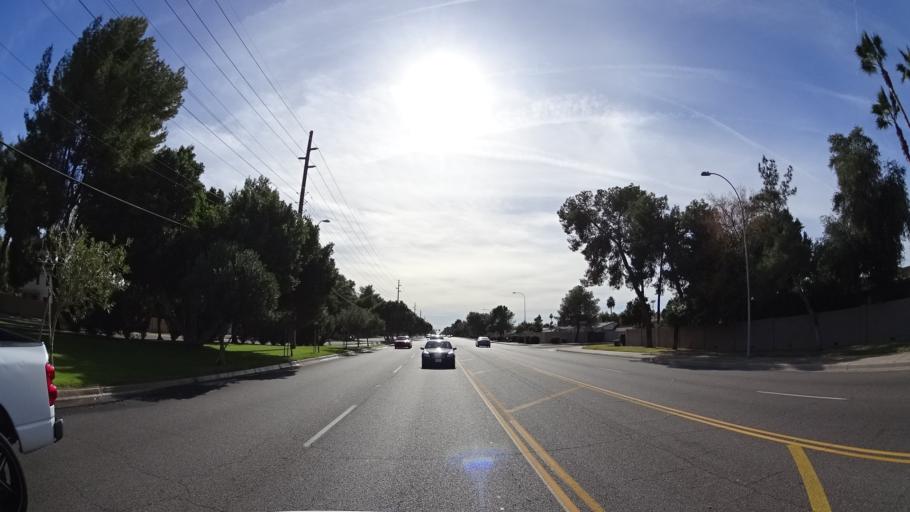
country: US
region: Arizona
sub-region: Maricopa County
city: Guadalupe
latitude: 33.3757
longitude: -111.9278
